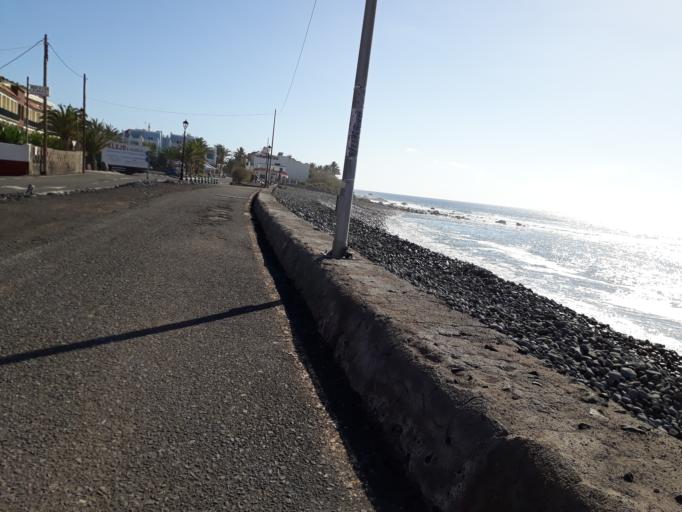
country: ES
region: Canary Islands
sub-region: Provincia de Santa Cruz de Tenerife
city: Alajero
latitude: 28.0900
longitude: -17.3395
